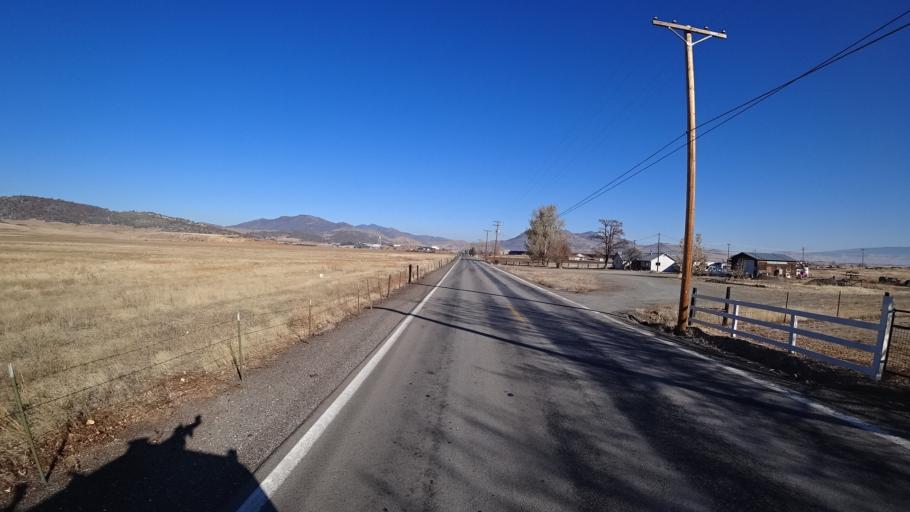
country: US
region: California
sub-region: Siskiyou County
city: Yreka
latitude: 41.7223
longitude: -122.5934
